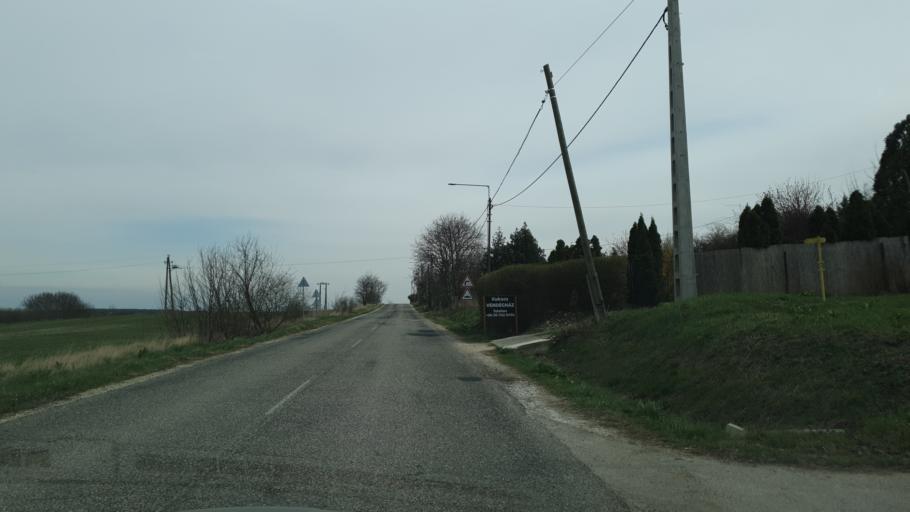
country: HU
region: Fejer
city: Etyek
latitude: 47.4541
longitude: 18.7337
